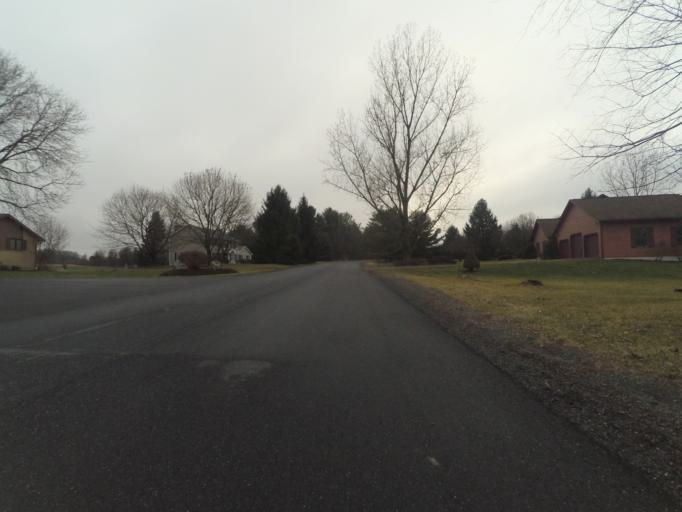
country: US
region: Pennsylvania
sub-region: Centre County
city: Park Forest Village
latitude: 40.7820
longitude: -77.9142
